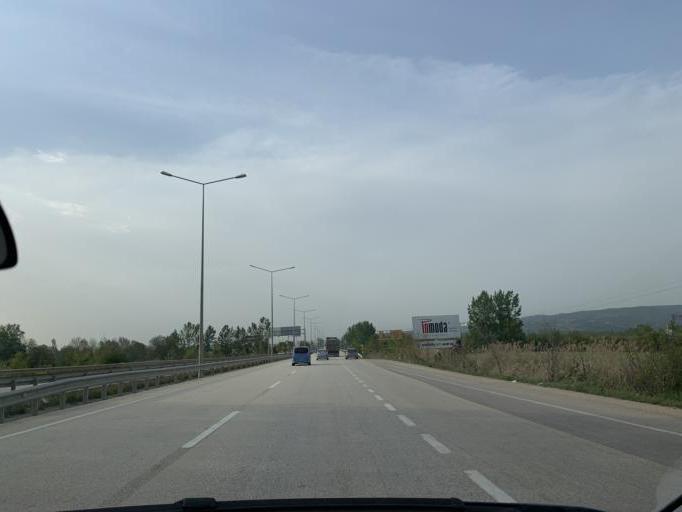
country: TR
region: Bursa
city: Kursunlu
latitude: 40.0444
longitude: 29.5914
